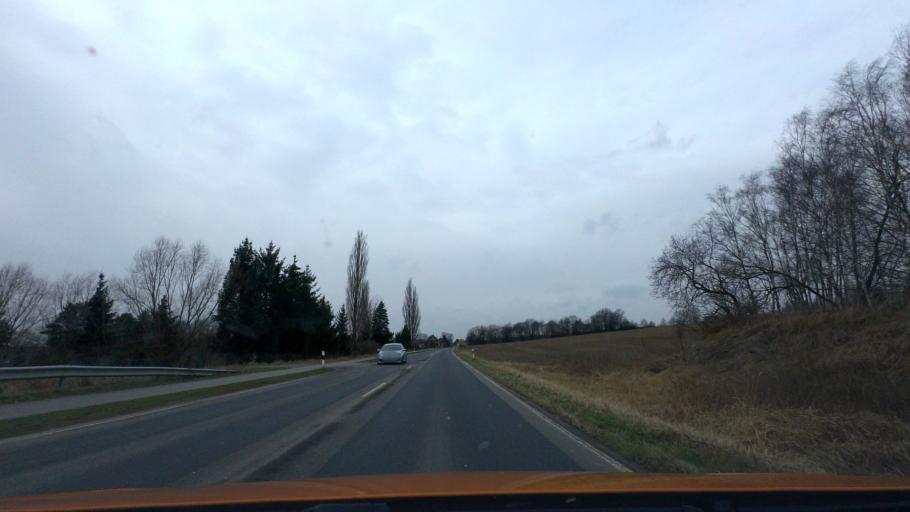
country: DE
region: Lower Saxony
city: Cremlingen
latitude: 52.2533
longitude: 10.6274
